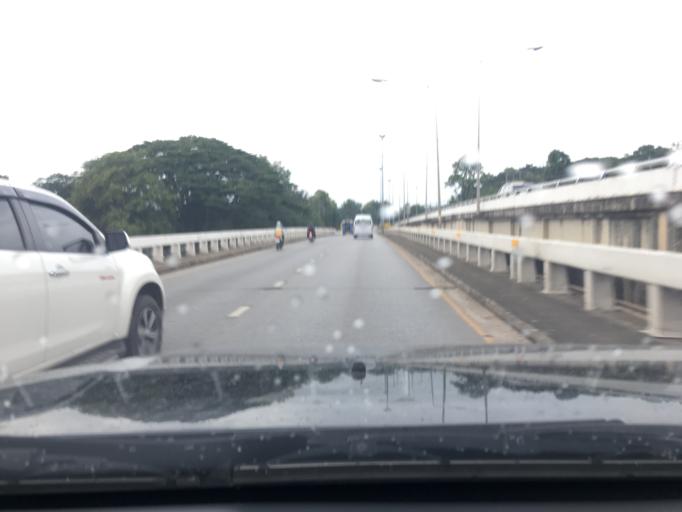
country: TH
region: Chiang Rai
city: Chiang Rai
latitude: 19.9215
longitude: 99.8459
